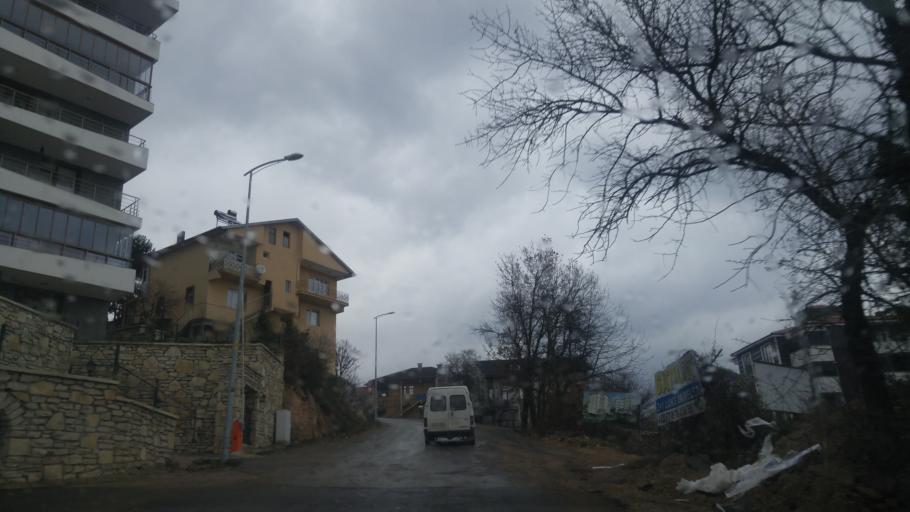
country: TR
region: Karabuk
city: Safranbolu
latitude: 41.2700
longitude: 32.6786
